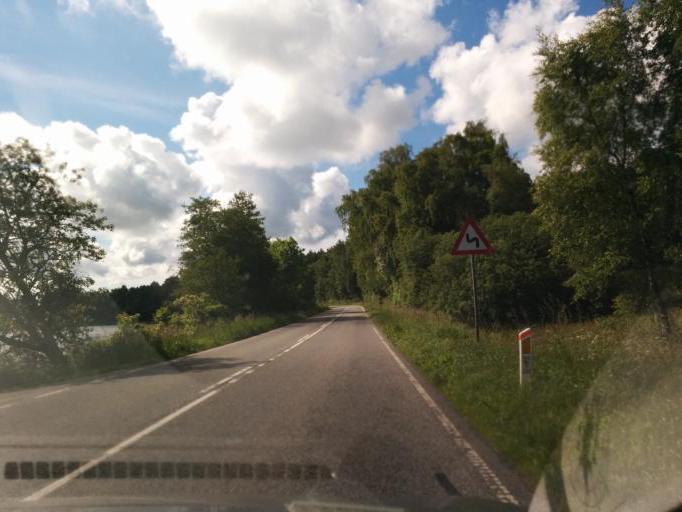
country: DK
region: Central Jutland
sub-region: Syddjurs Kommune
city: Ebeltoft
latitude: 56.2668
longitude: 10.6089
